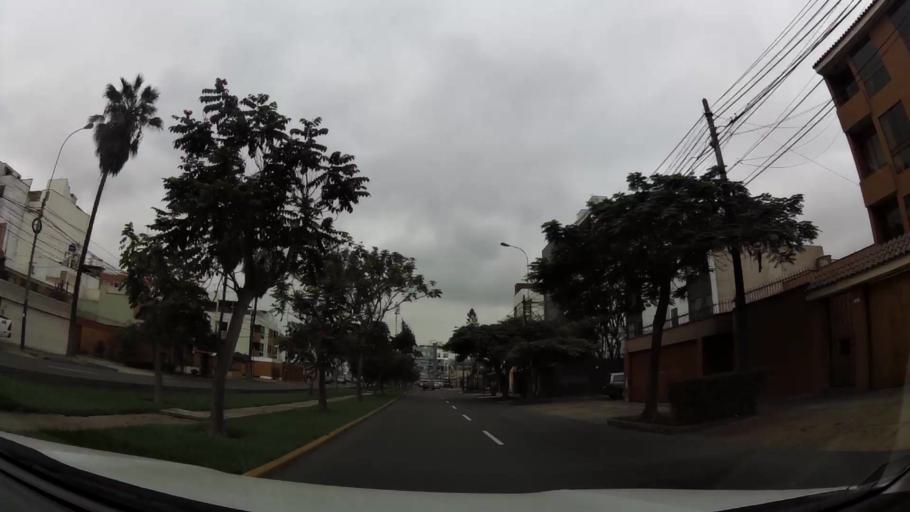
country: PE
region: Lima
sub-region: Lima
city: Surco
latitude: -12.1232
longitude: -76.9915
